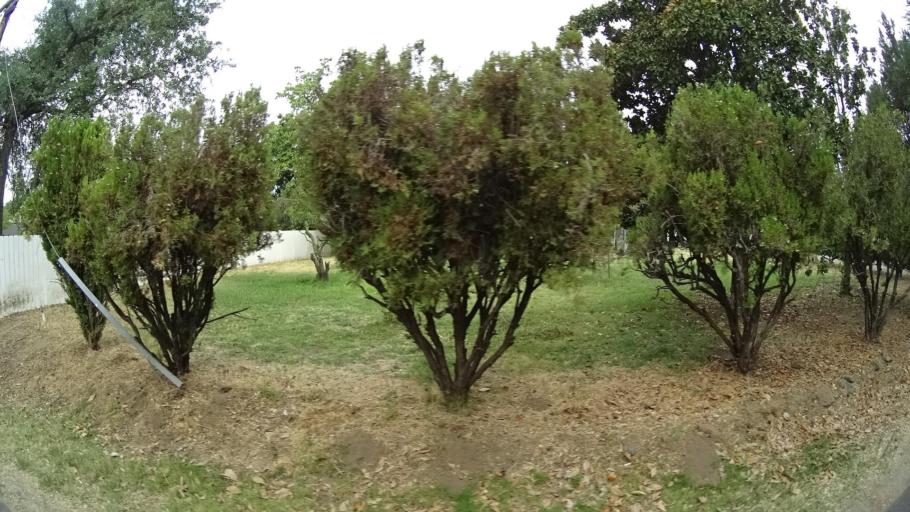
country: US
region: California
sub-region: Placer County
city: Loomis
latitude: 38.8119
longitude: -121.1916
